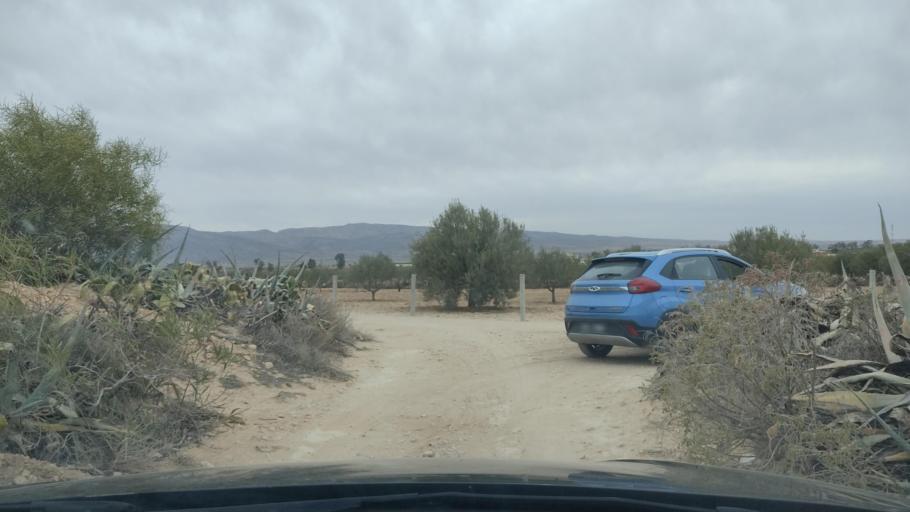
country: TN
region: Al Qasrayn
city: Kasserine
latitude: 35.2252
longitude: 8.9236
